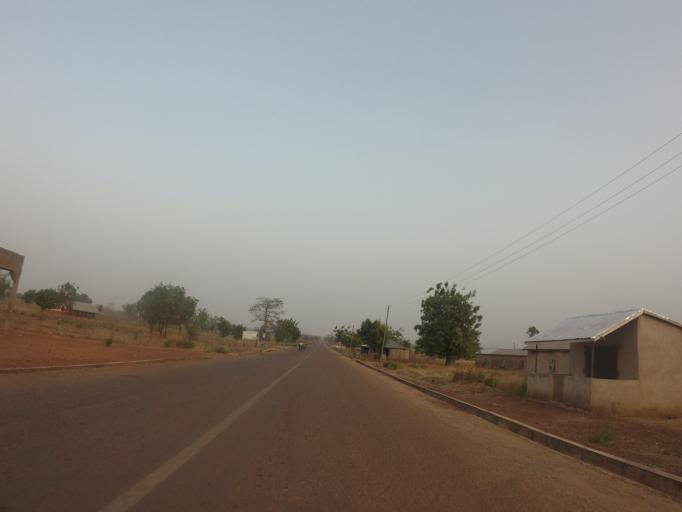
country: GH
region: Northern
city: Tamale
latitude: 9.4440
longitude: -1.1127
